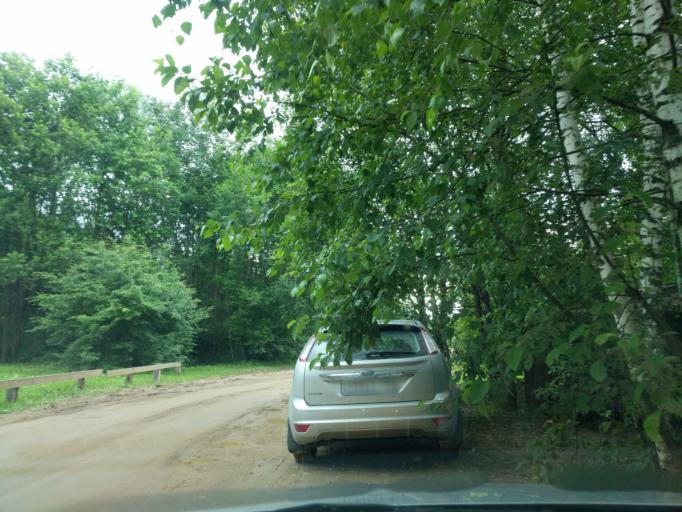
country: RU
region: Kaluga
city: Nikola-Lenivets
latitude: 54.7609
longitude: 35.6004
